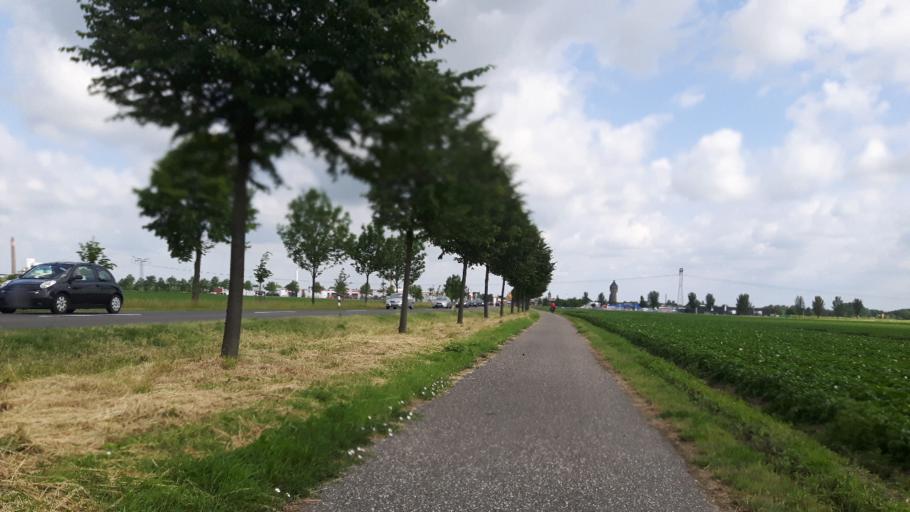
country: DE
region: Saxony
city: Dobernitz
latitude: 51.5066
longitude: 12.3392
